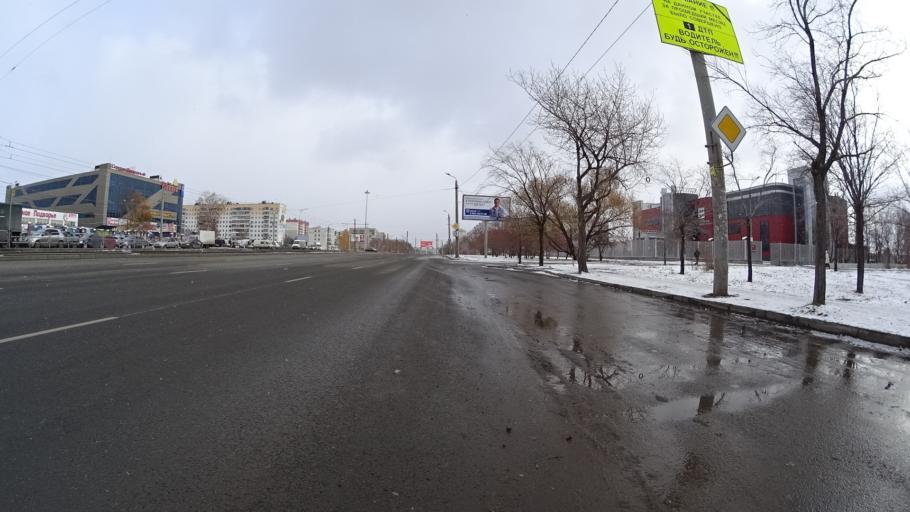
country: RU
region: Chelyabinsk
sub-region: Gorod Chelyabinsk
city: Chelyabinsk
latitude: 55.1887
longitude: 61.3181
